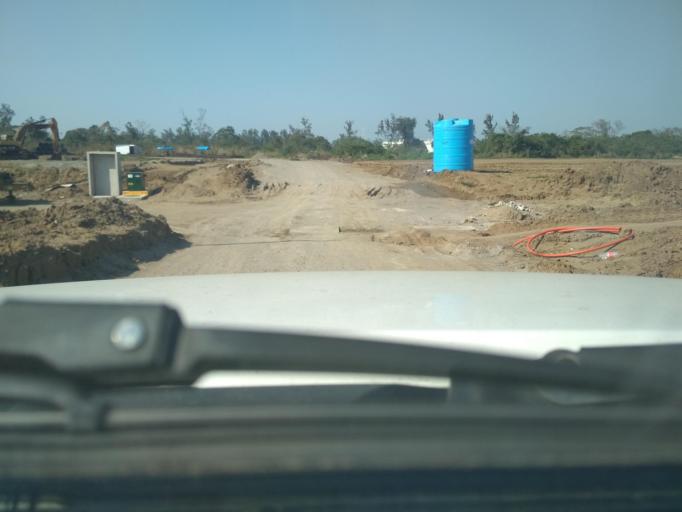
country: MX
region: Veracruz
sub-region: Veracruz
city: Las Amapolas
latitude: 19.1502
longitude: -96.2068
